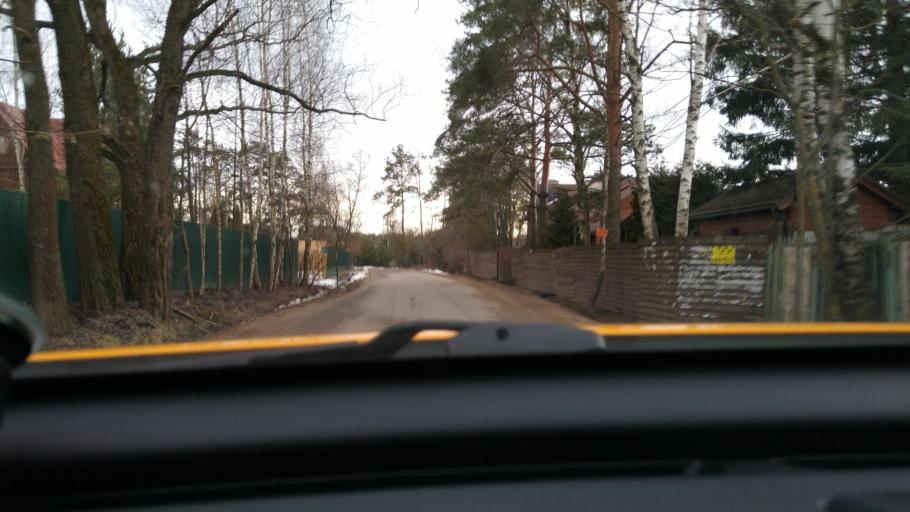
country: RU
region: Moskovskaya
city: Petrovo-Dal'neye
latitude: 55.7672
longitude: 37.2075
